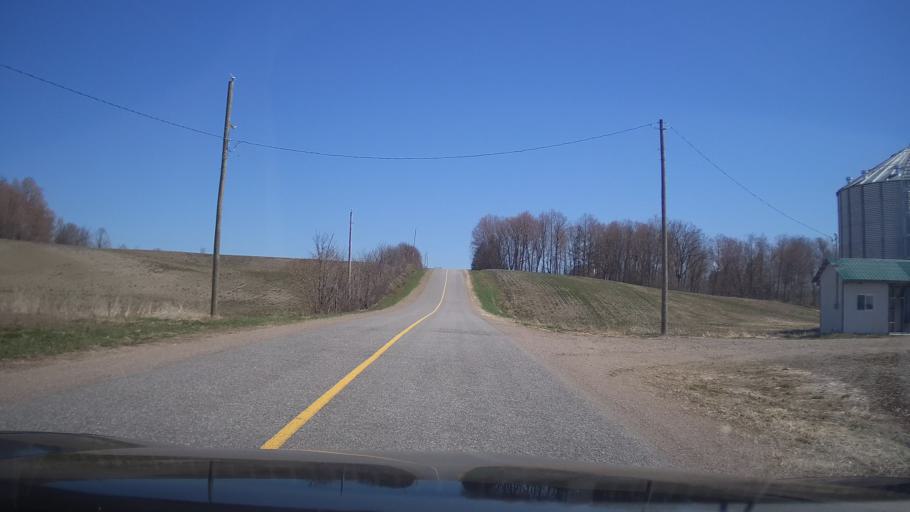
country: CA
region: Ontario
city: Arnprior
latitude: 45.5338
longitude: -76.3934
